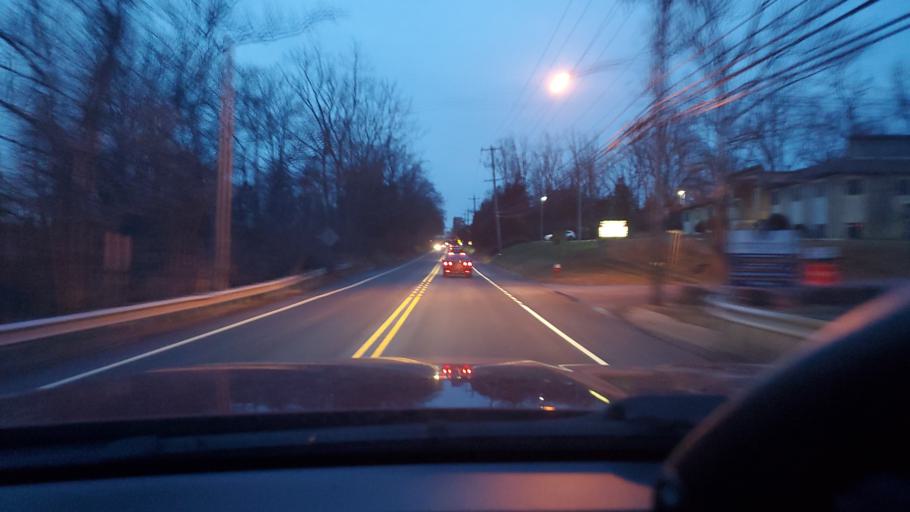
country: US
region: Pennsylvania
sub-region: Montgomery County
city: Spring Mount
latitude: 40.2729
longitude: -75.4736
